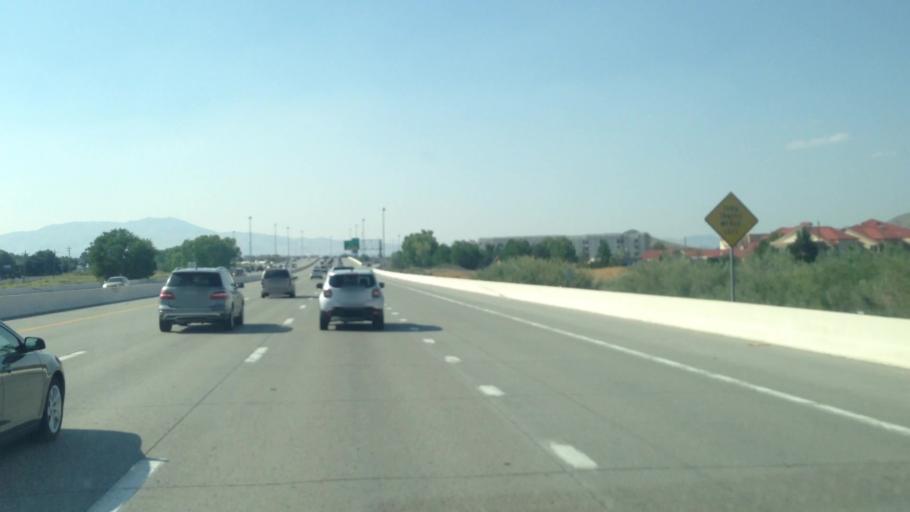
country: US
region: Nevada
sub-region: Washoe County
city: Sparks
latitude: 39.4327
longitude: -119.7604
